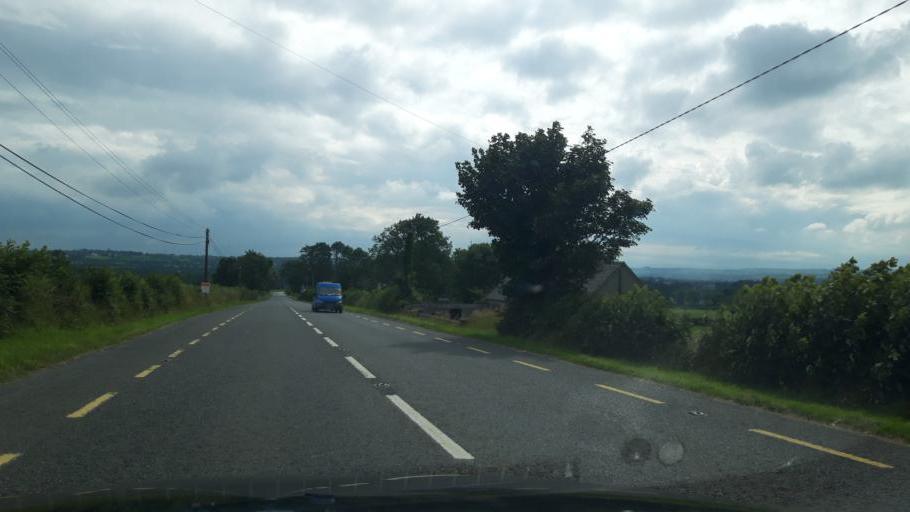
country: IE
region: Leinster
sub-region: Kilkenny
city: Castlecomer
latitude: 52.8544
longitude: -7.1186
